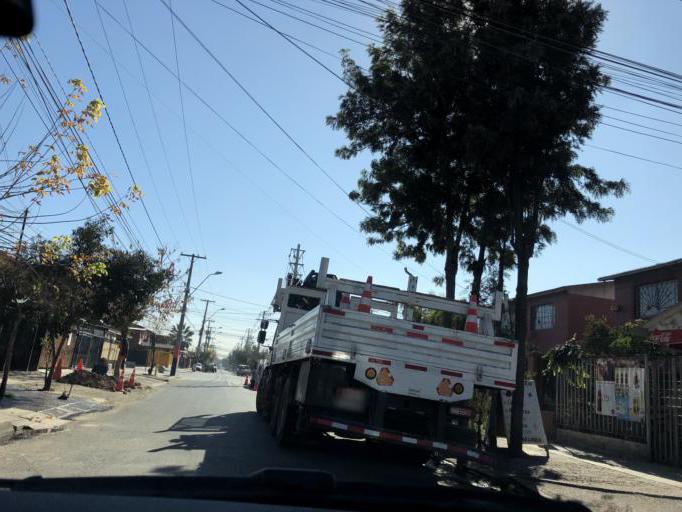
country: CL
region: Santiago Metropolitan
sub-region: Provincia de Cordillera
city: Puente Alto
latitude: -33.6215
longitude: -70.6108
